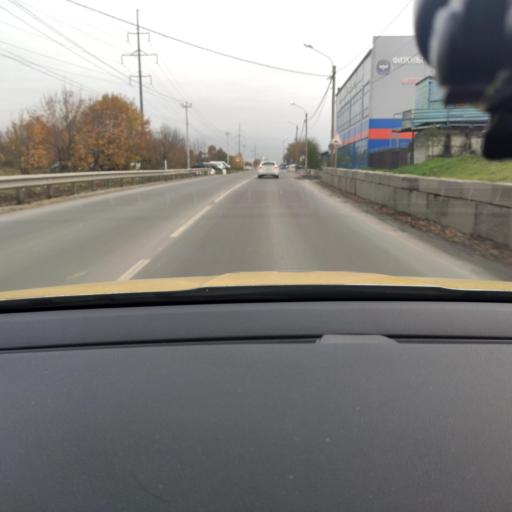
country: RU
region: Moskovskaya
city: Mosrentgen
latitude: 55.6100
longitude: 37.4586
